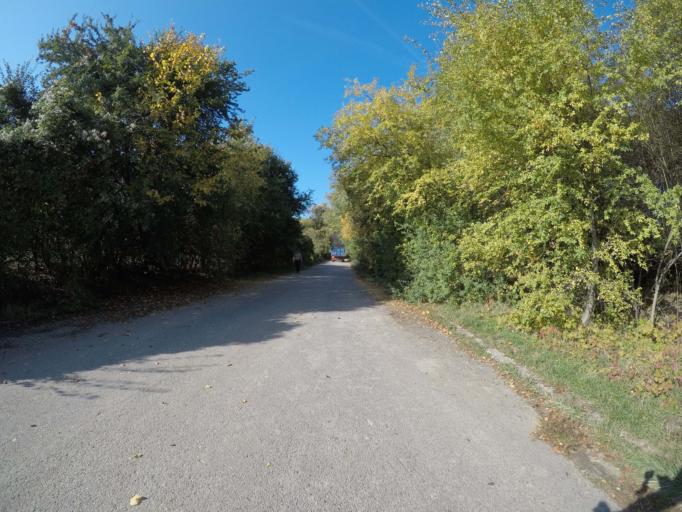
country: SK
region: Trenciansky
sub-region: Okres Nove Mesto nad Vahom
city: Nove Mesto nad Vahom
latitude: 48.7554
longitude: 17.8097
